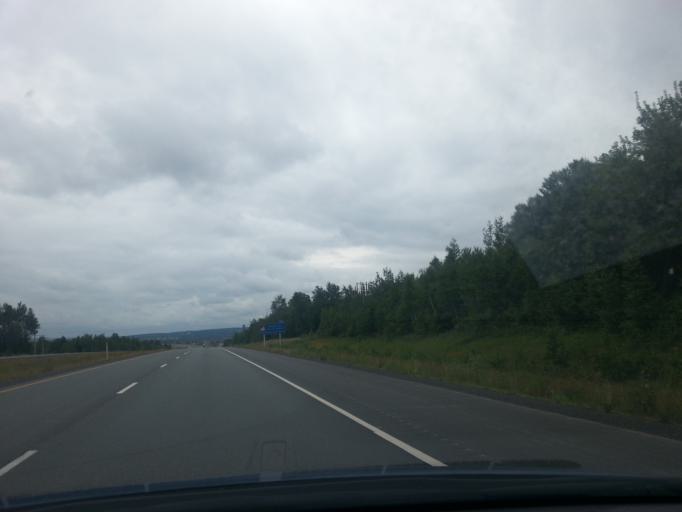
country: CA
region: New Brunswick
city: Harrison Brook
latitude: 47.2046
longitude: -67.9308
